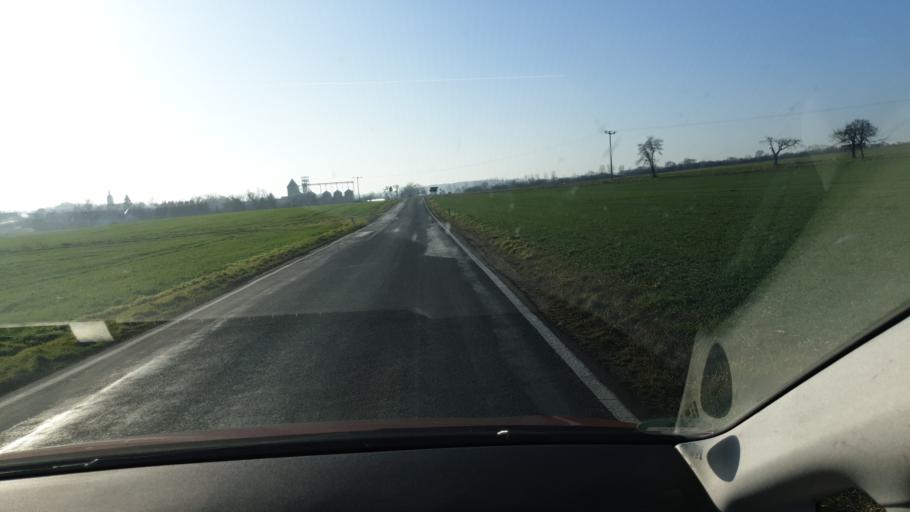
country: DE
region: Saxony
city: Hohburg
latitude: 51.4612
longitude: 12.7860
